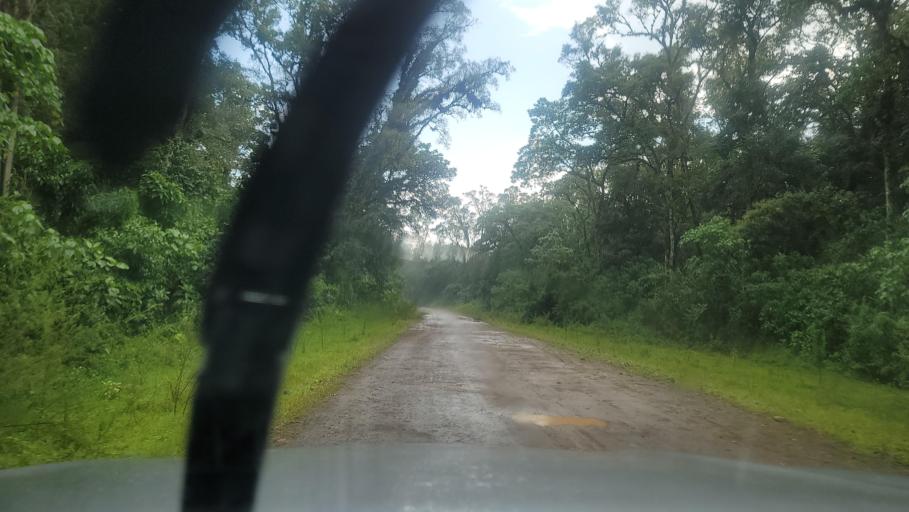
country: ET
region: Southern Nations, Nationalities, and People's Region
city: Bonga
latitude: 7.6551
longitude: 36.2470
